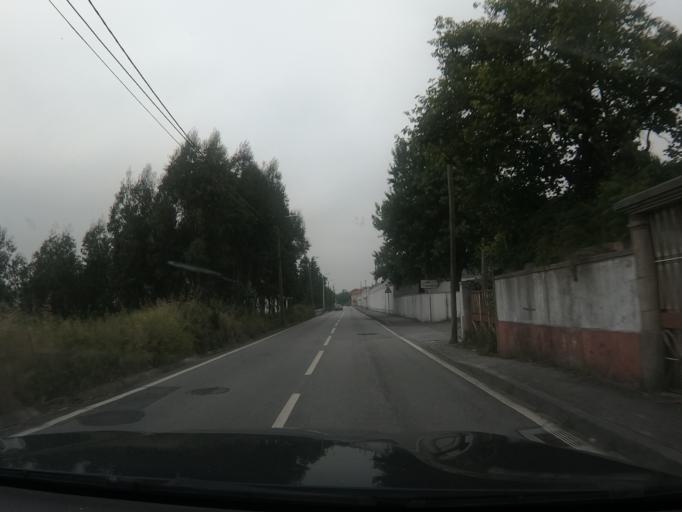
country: PT
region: Aveiro
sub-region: Santa Maria da Feira
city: Lamas
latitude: 41.0030
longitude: -8.5641
